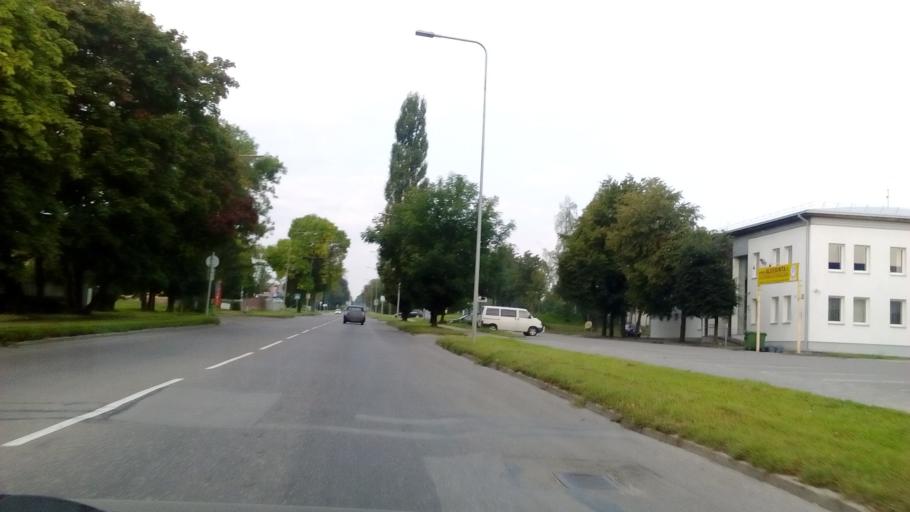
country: LT
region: Alytaus apskritis
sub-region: Alytus
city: Alytus
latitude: 54.3870
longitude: 24.0374
